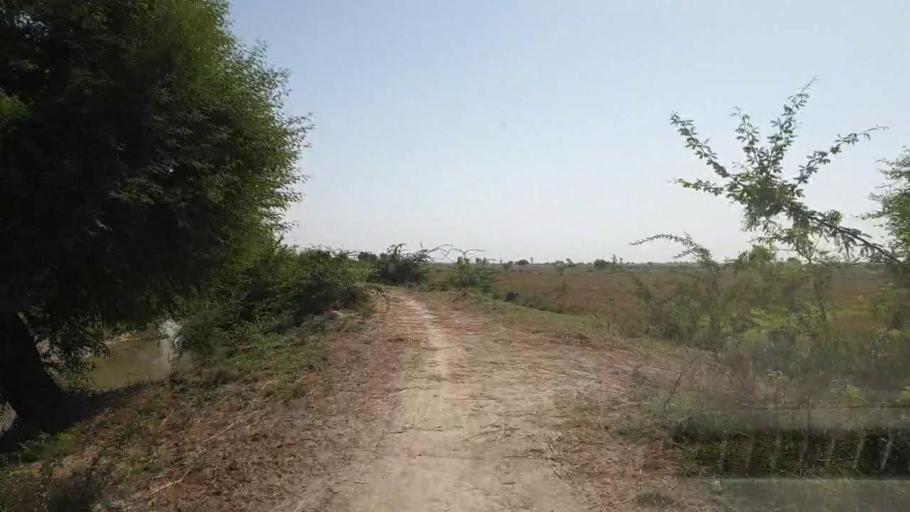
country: PK
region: Sindh
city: Kadhan
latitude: 24.6250
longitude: 68.9946
